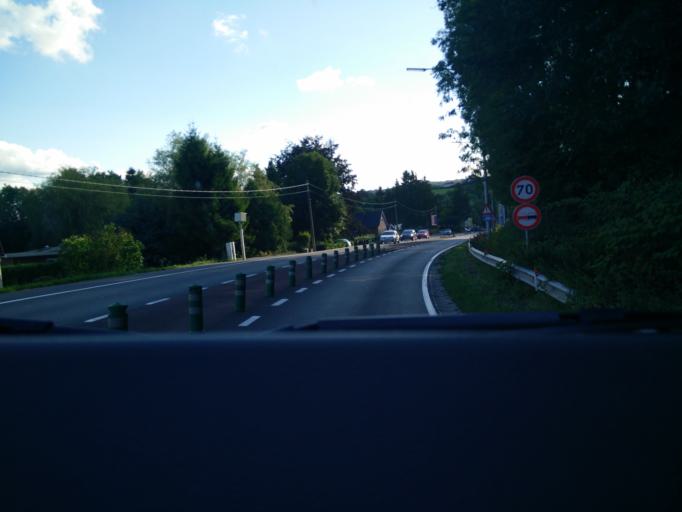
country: BE
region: Wallonia
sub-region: Province du Hainaut
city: Beaumont
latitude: 50.2316
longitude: 4.2369
